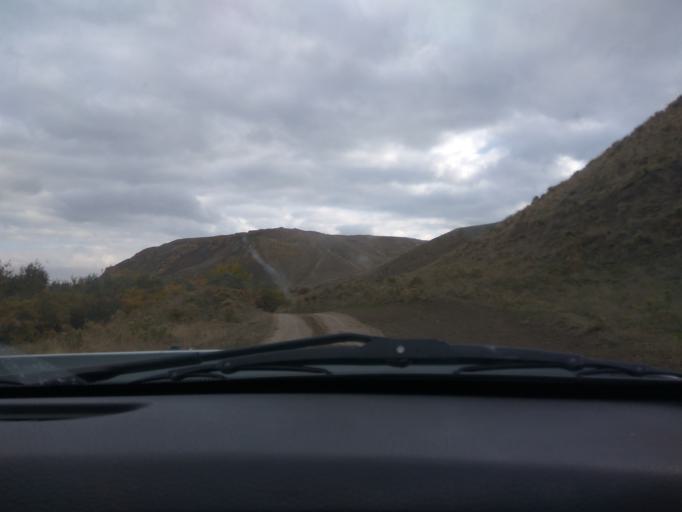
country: RU
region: Dagestan
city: Korkmaskala
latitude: 42.9981
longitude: 47.2346
